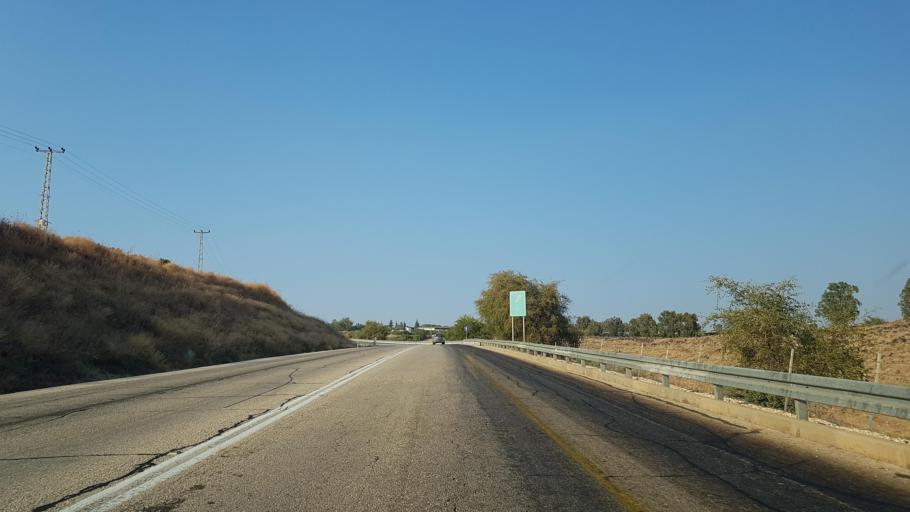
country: SY
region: Quneitra
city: Al Butayhah
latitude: 32.9010
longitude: 35.5971
